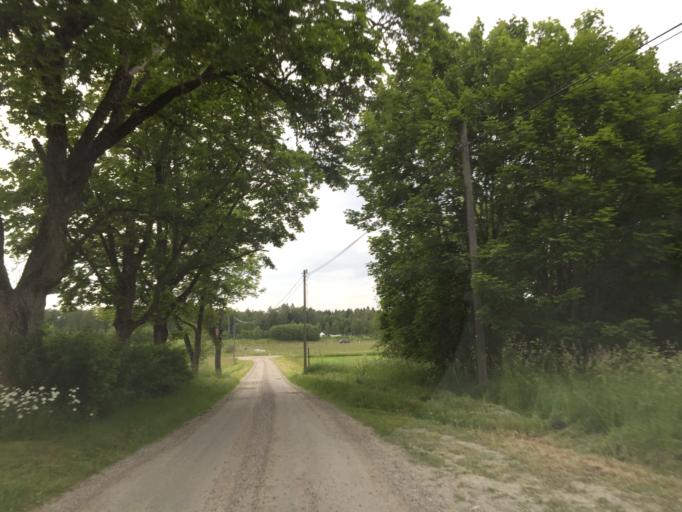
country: SE
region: OErebro
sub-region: Lindesbergs Kommun
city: Fellingsbro
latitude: 59.3310
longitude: 15.5295
